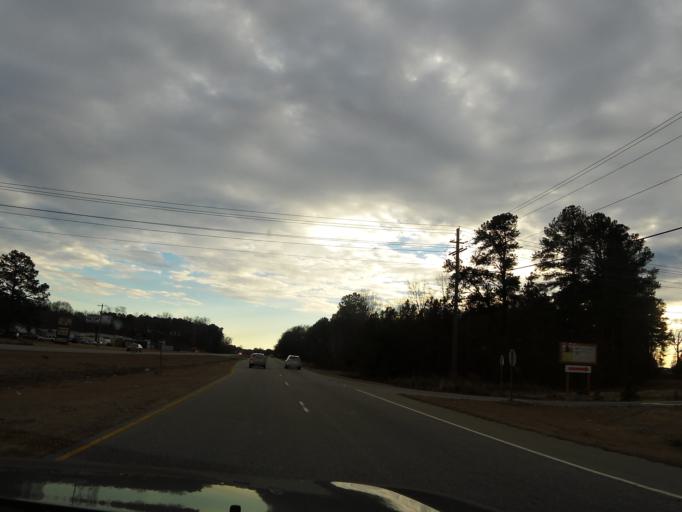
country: US
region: North Carolina
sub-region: Nash County
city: Rocky Mount
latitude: 35.9313
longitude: -77.8305
